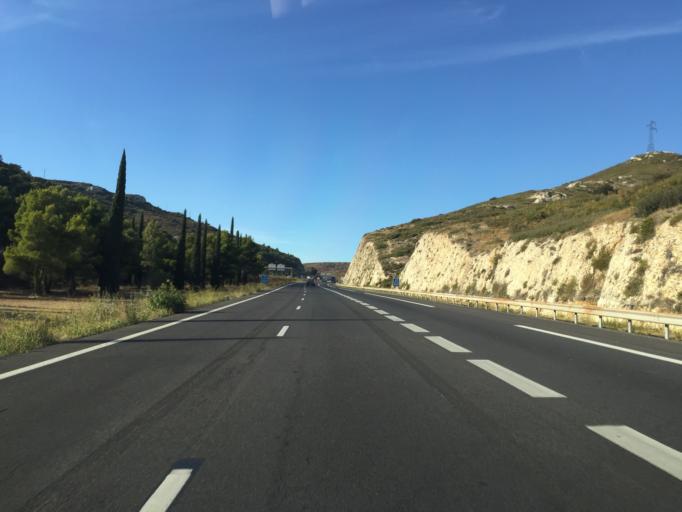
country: FR
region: Provence-Alpes-Cote d'Azur
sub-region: Departement des Bouches-du-Rhone
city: Coudoux
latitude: 43.5582
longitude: 5.2305
